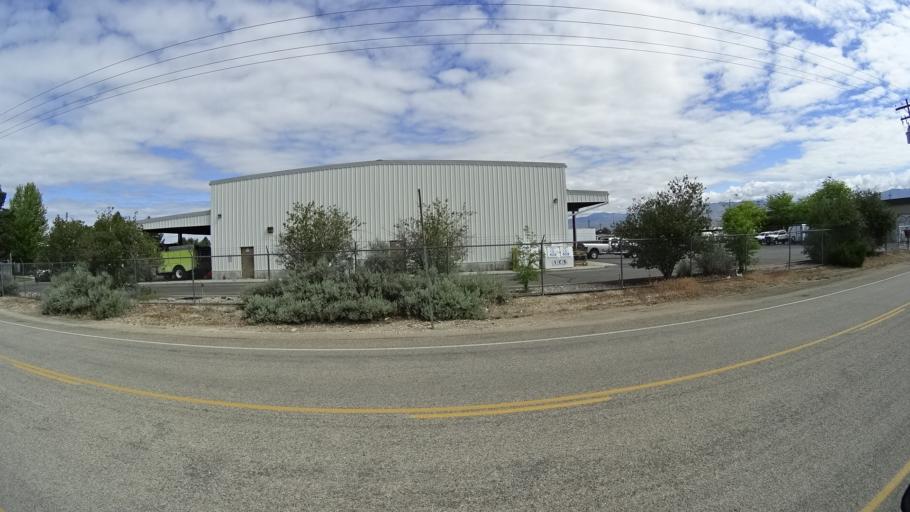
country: US
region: Idaho
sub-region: Ada County
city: Boise
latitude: 43.5641
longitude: -116.2058
